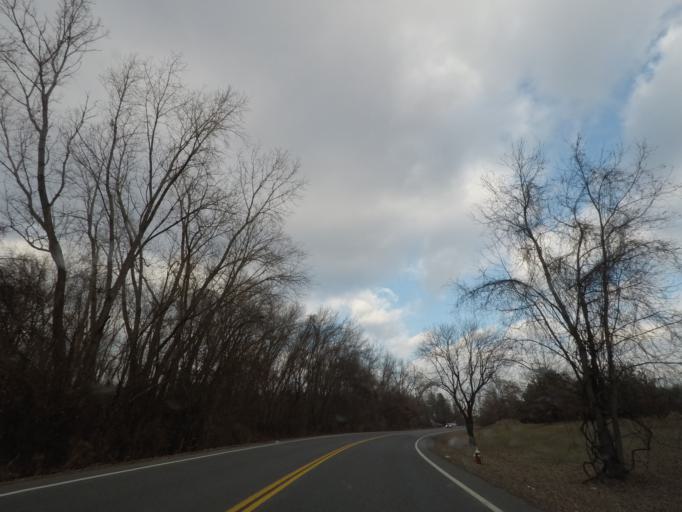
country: US
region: New York
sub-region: Albany County
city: Westmere
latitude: 42.6927
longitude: -73.8567
